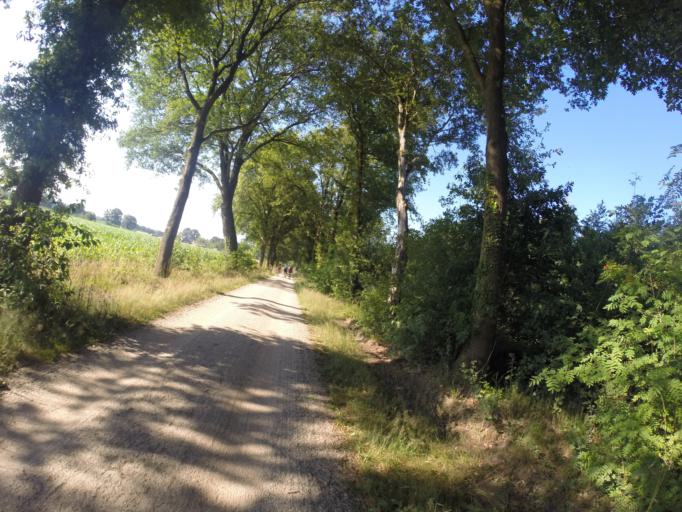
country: NL
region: Gelderland
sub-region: Gemeente Bronckhorst
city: Hengelo
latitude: 52.0880
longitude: 6.3543
